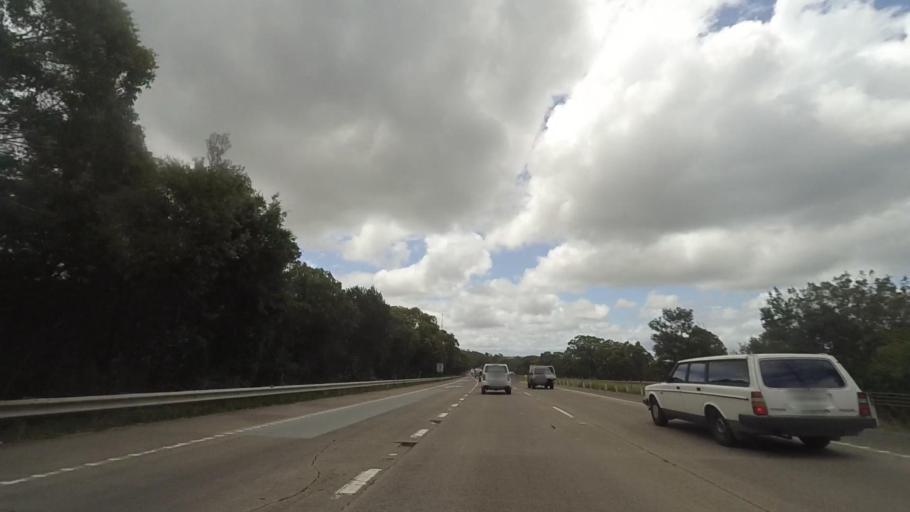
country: AU
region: New South Wales
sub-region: Gosford Shire
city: Point Clare
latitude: -33.4055
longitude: 151.2985
